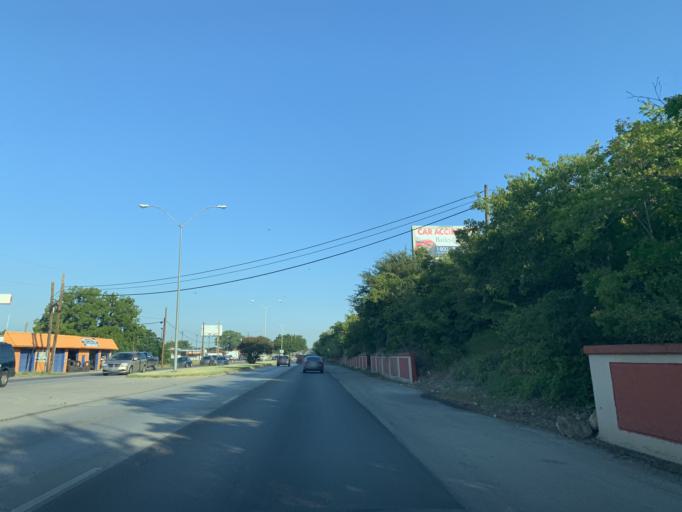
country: US
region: Texas
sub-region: Tarrant County
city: River Oaks
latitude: 32.7697
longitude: -97.3582
